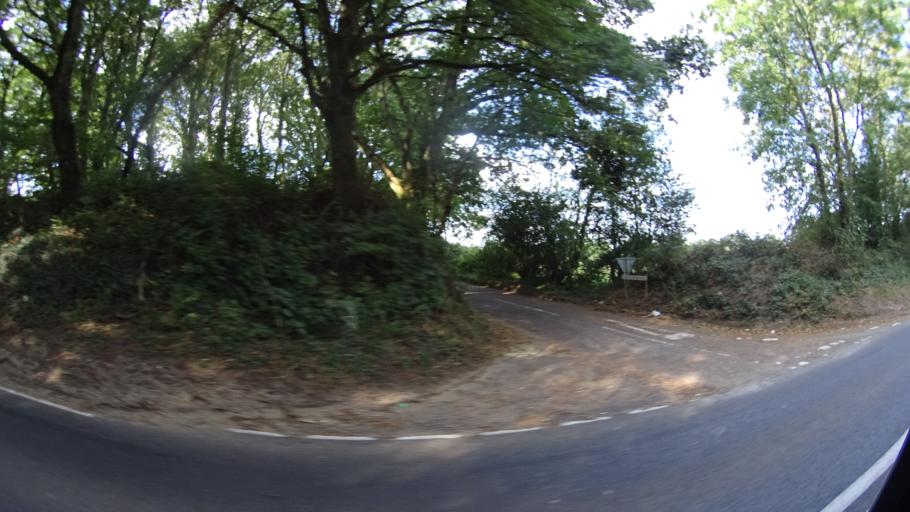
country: GB
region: England
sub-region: Dorset
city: Lytchett Matravers
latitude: 50.7699
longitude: -2.0660
